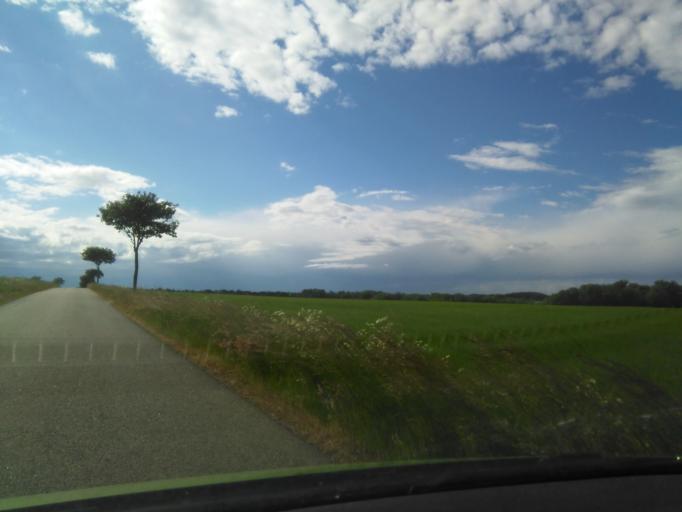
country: DK
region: Capital Region
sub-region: Bornholm Kommune
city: Nexo
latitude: 55.1252
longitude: 15.0606
